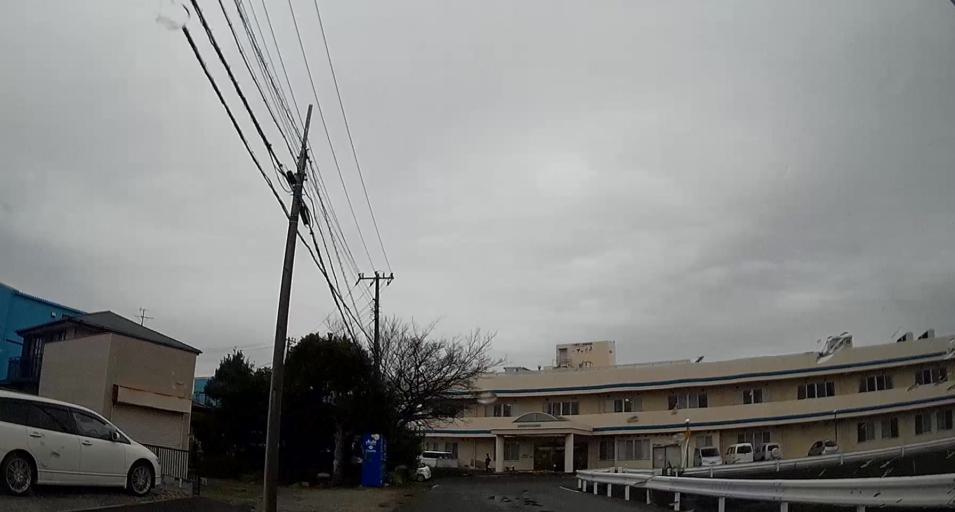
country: JP
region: Chiba
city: Kisarazu
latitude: 35.4369
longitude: 139.9201
